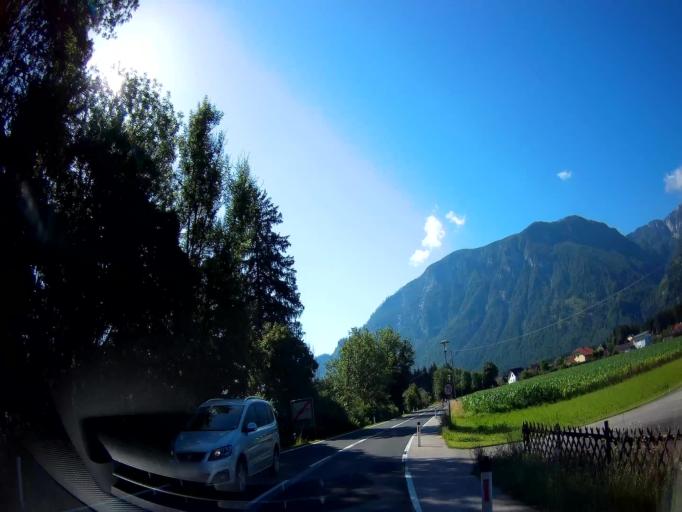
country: AT
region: Carinthia
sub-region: Politischer Bezirk Volkermarkt
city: Gallizien
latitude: 46.5569
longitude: 14.5114
